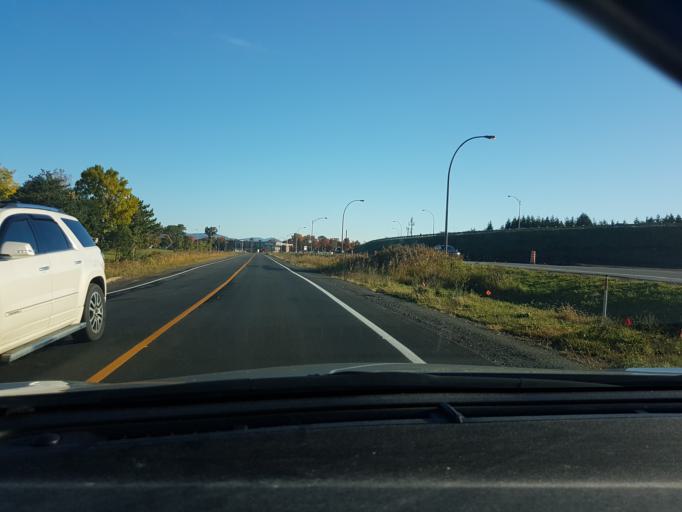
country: CA
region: Quebec
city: L'Ancienne-Lorette
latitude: 46.7889
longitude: -71.3175
